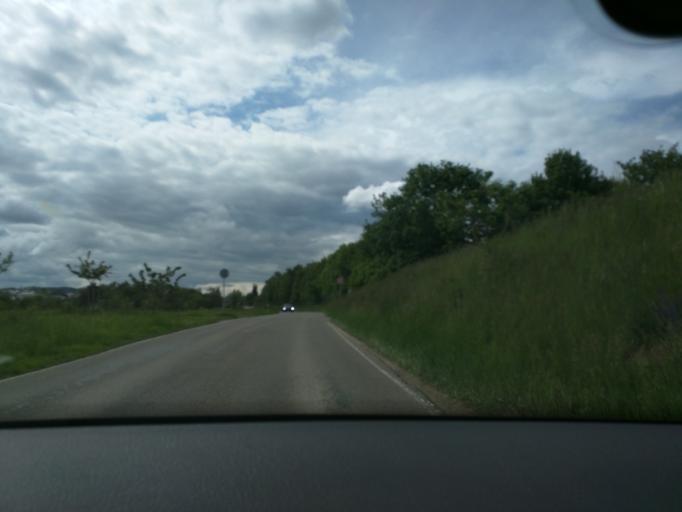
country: DE
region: Baden-Wuerttemberg
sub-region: Tuebingen Region
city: Rottenburg
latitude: 48.5034
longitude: 8.9464
